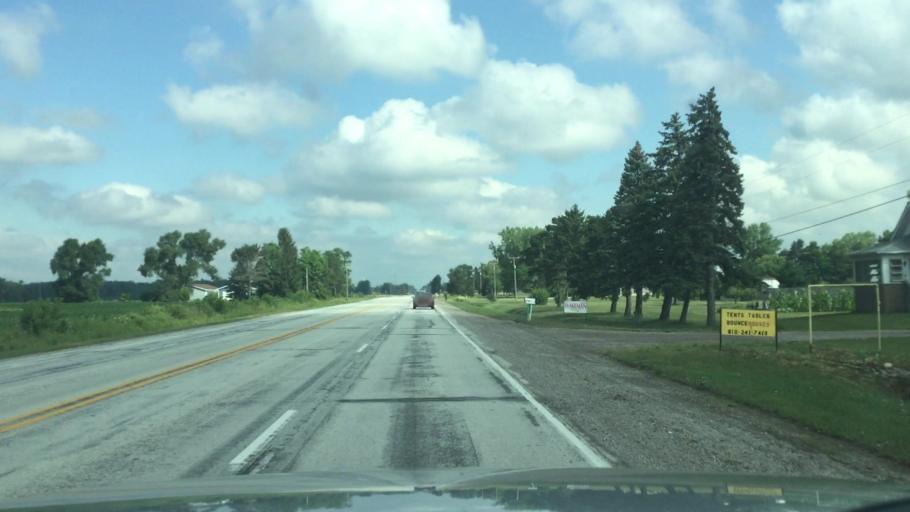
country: US
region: Michigan
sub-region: Saginaw County
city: Birch Run
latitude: 43.2314
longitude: -83.7551
